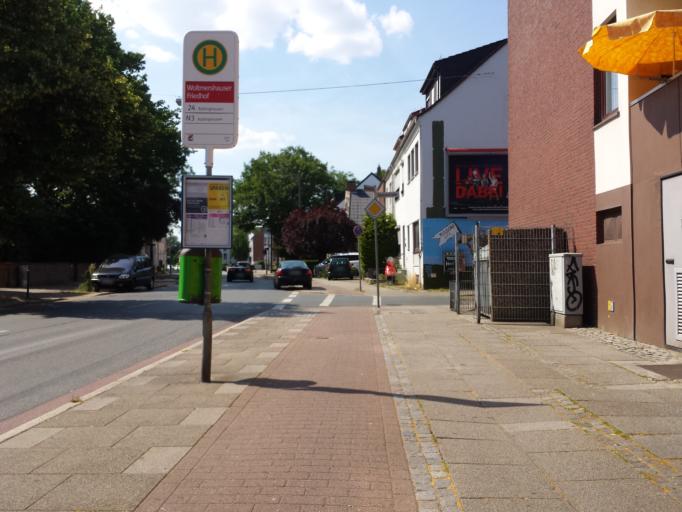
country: DE
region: Bremen
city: Bremen
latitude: 53.0875
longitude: 8.7617
